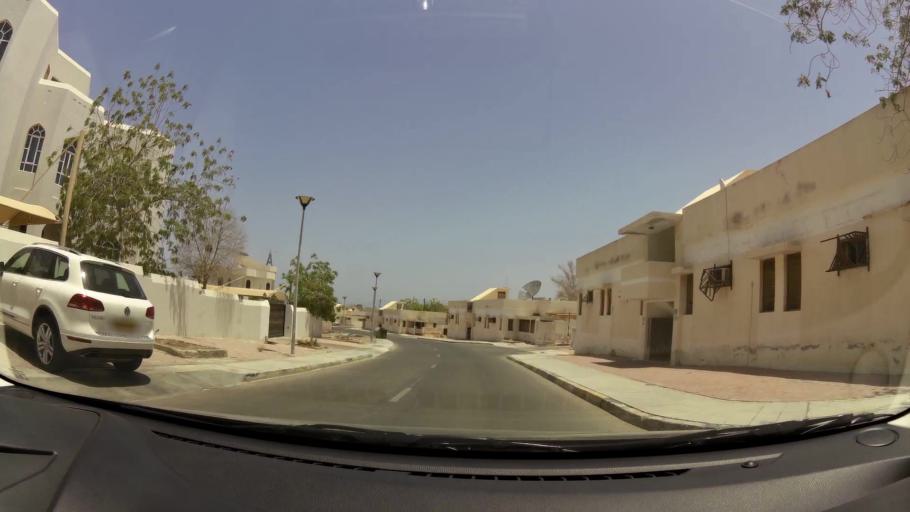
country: OM
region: Muhafazat Masqat
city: Bawshar
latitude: 23.6062
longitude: 58.4686
